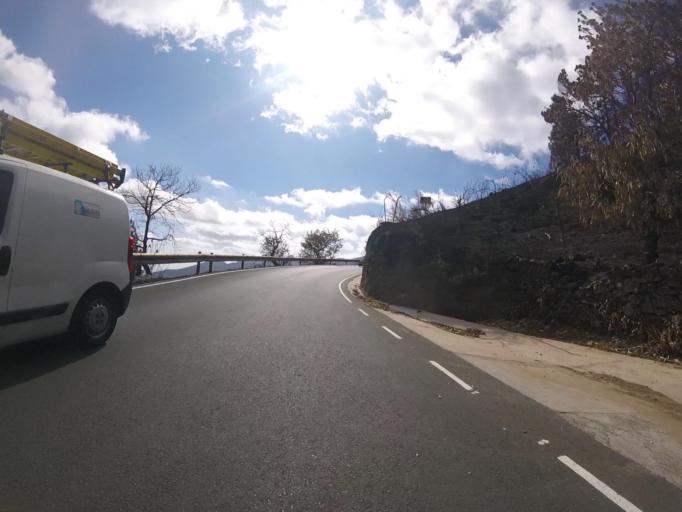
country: ES
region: Canary Islands
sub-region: Provincia de Las Palmas
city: Tejeda
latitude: 28.0018
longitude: -15.5942
